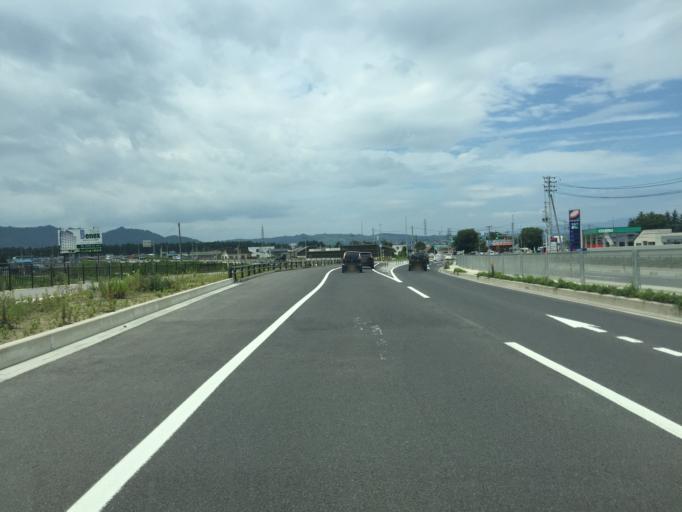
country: JP
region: Yamagata
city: Yonezawa
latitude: 37.8990
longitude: 140.1423
